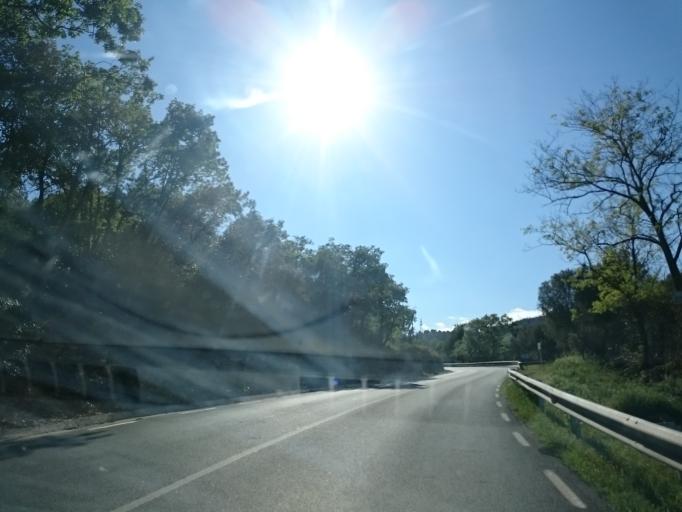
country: ES
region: Catalonia
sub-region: Provincia de Barcelona
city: Sant Boi de Llobregat
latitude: 41.3457
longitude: 2.0183
